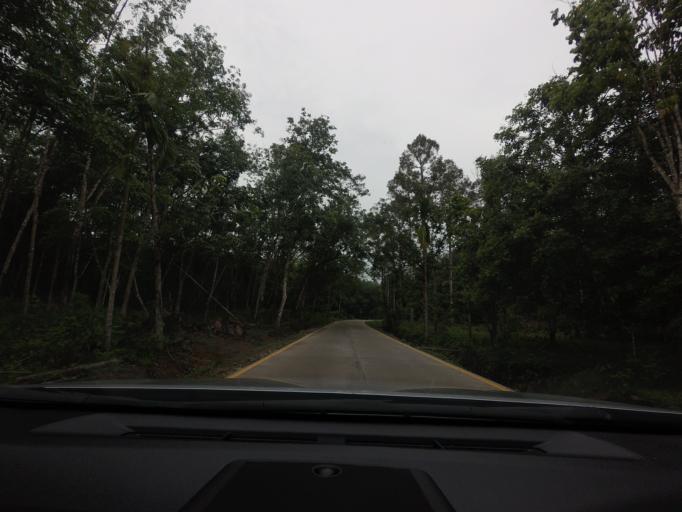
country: TH
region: Narathiwat
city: Rueso
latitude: 6.4113
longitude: 101.5268
